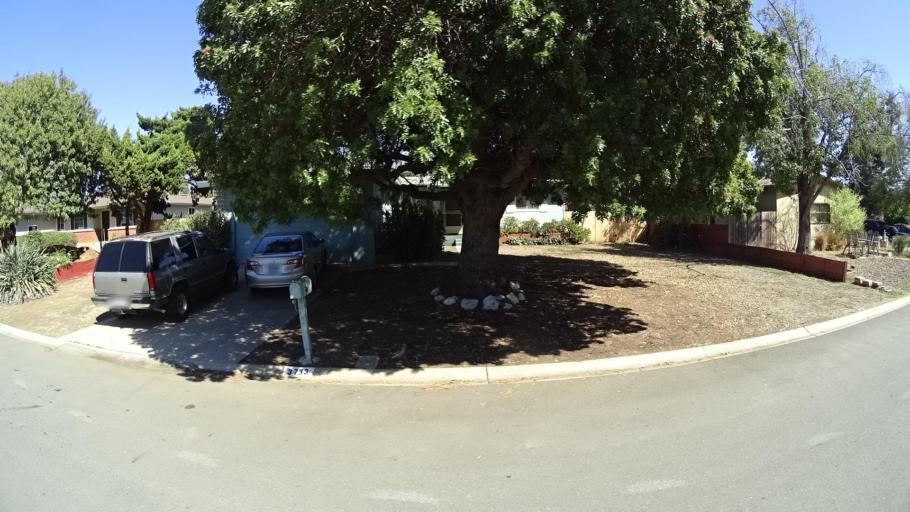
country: US
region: California
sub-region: San Diego County
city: Bonita
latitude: 32.6557
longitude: -117.0577
